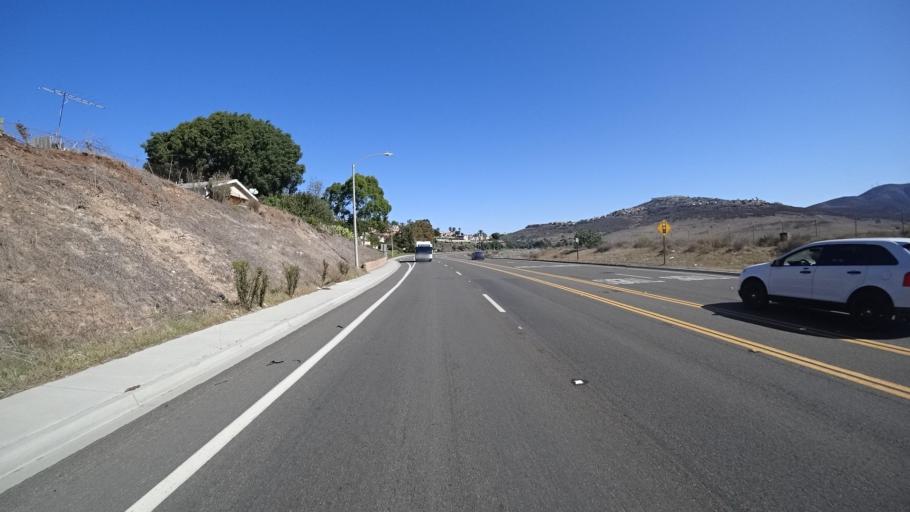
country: US
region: California
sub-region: San Diego County
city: La Presa
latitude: 32.7115
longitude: -116.9818
